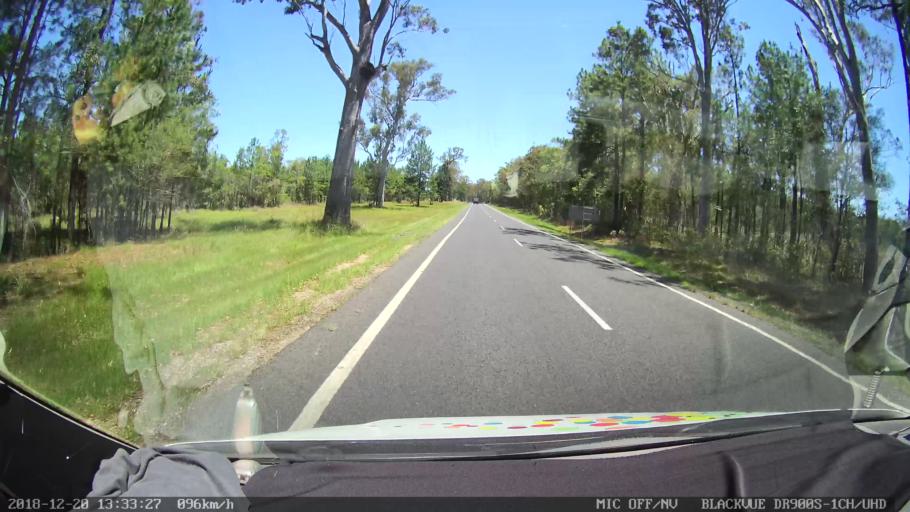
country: AU
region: New South Wales
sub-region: Clarence Valley
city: Gordon
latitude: -29.2457
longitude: 152.9864
